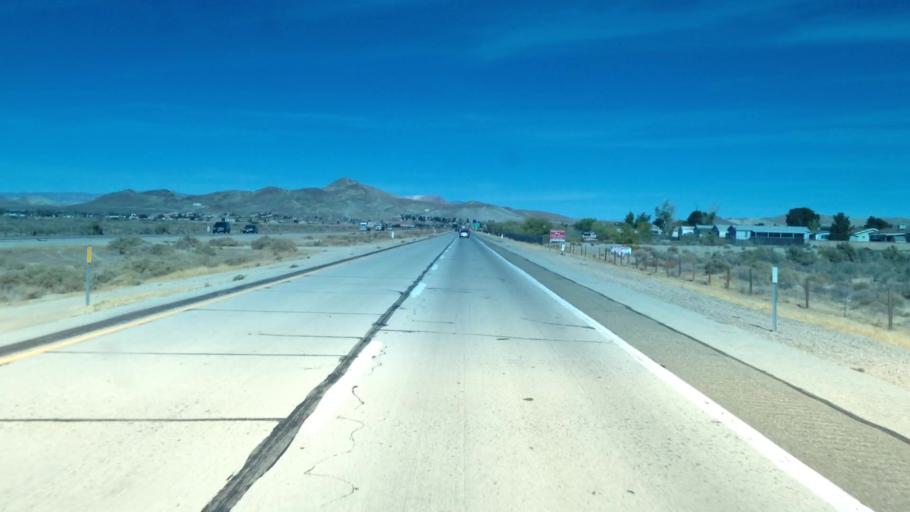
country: US
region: California
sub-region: Kern County
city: Rosamond
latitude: 34.8412
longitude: -118.1708
